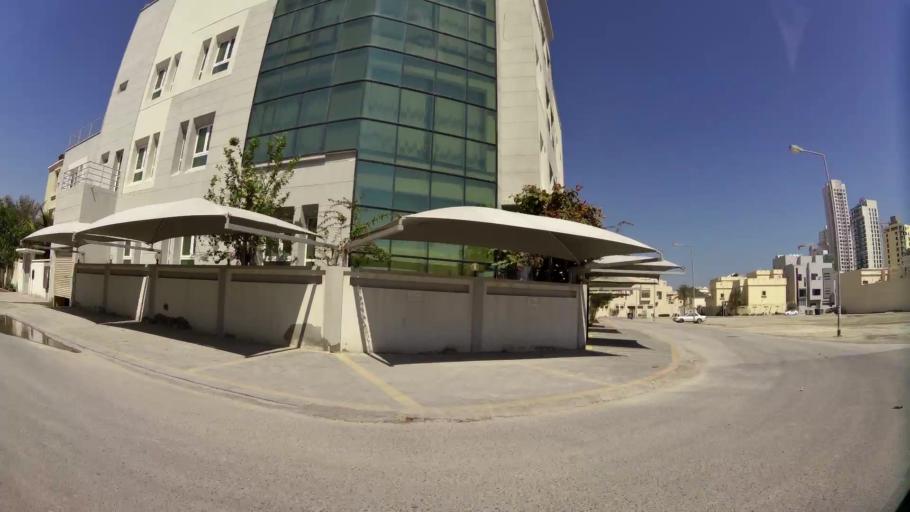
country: BH
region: Manama
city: Manama
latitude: 26.2110
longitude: 50.6154
